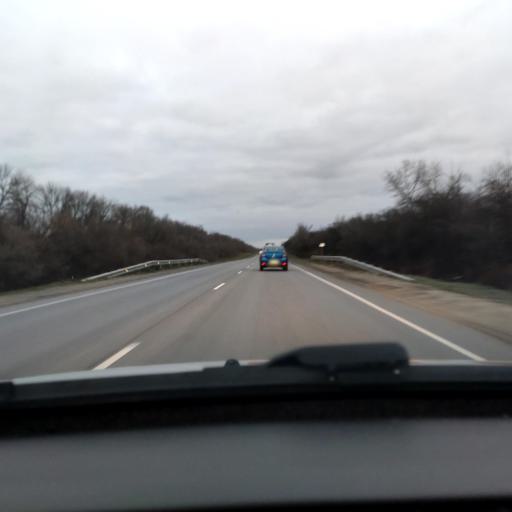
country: RU
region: Lipetsk
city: Borinskoye
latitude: 52.4372
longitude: 39.2757
